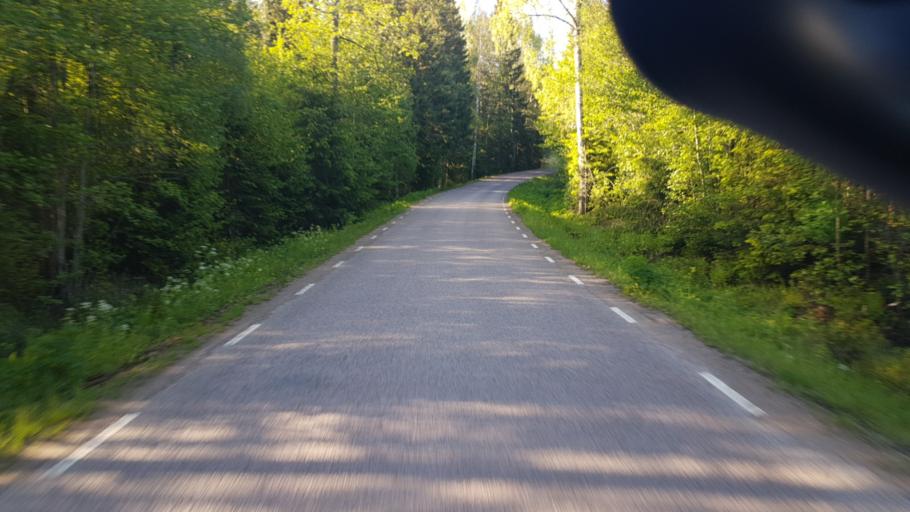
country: SE
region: Vaermland
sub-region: Arvika Kommun
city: Arvika
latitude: 59.5448
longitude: 12.5189
